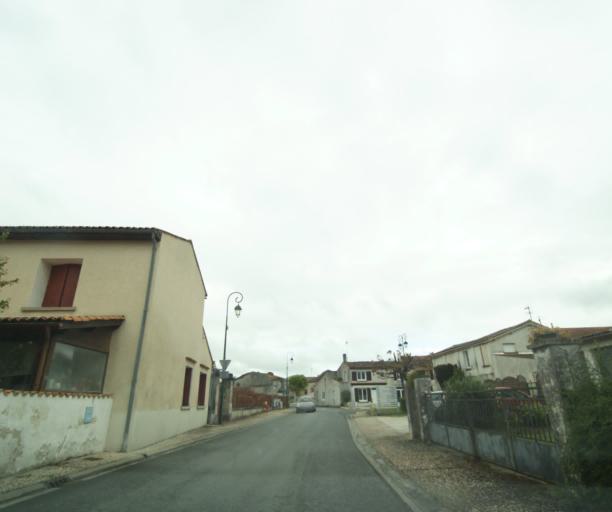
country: FR
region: Poitou-Charentes
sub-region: Departement de la Charente-Maritime
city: Perignac
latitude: 45.6484
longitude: -0.5058
